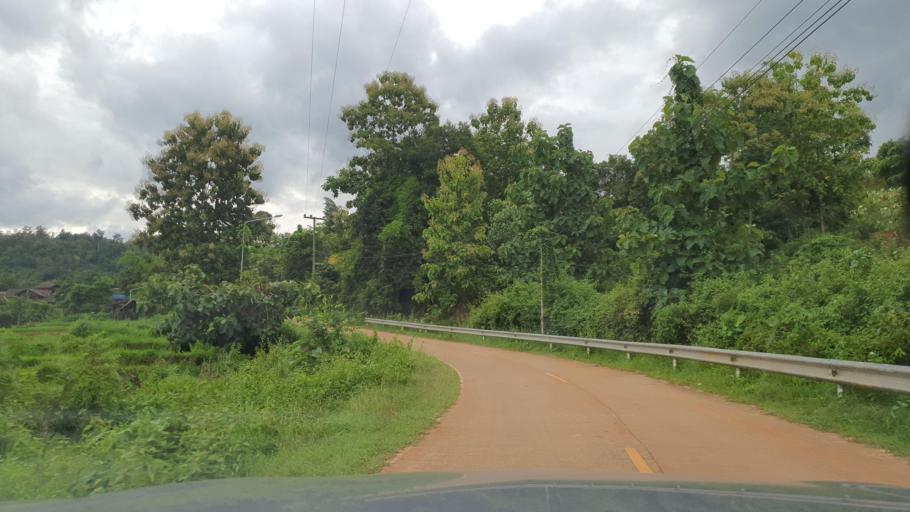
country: TH
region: Chiang Mai
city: Mae Wang
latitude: 18.6687
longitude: 98.6267
